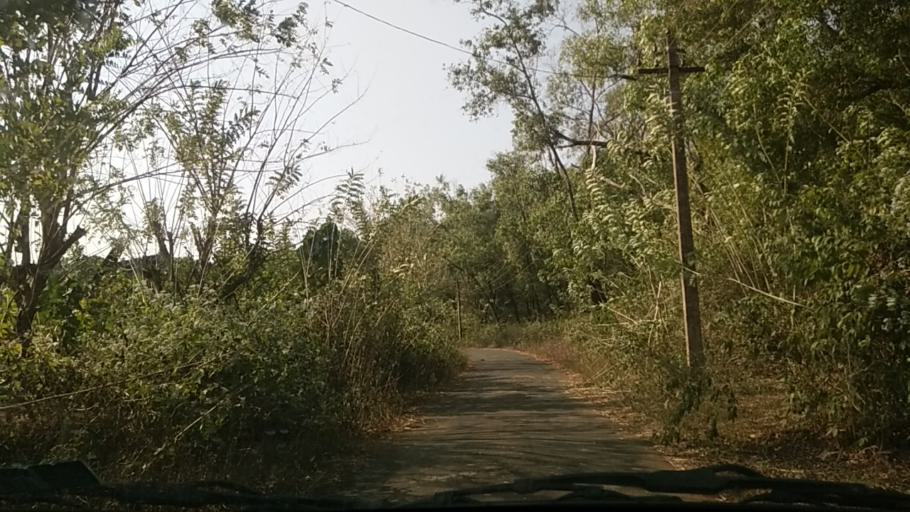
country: IN
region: Goa
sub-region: North Goa
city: Ponda
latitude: 15.3779
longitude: 74.0855
